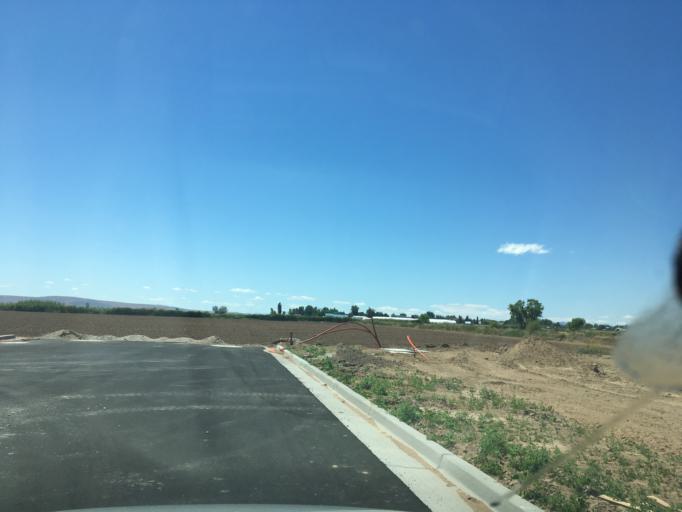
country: US
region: Utah
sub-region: Davis County
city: Layton
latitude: 41.0541
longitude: -112.0145
